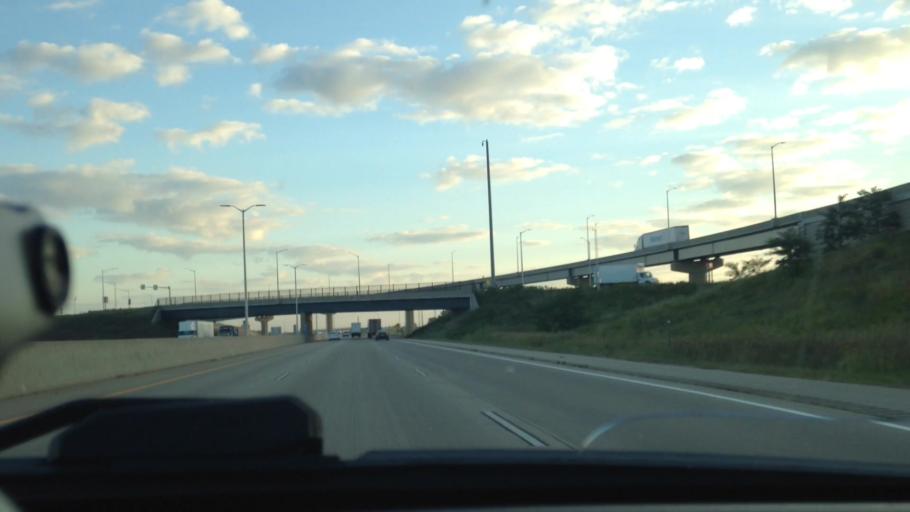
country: US
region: Wisconsin
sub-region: Winnebago County
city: Oshkosh
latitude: 44.0577
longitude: -88.5747
